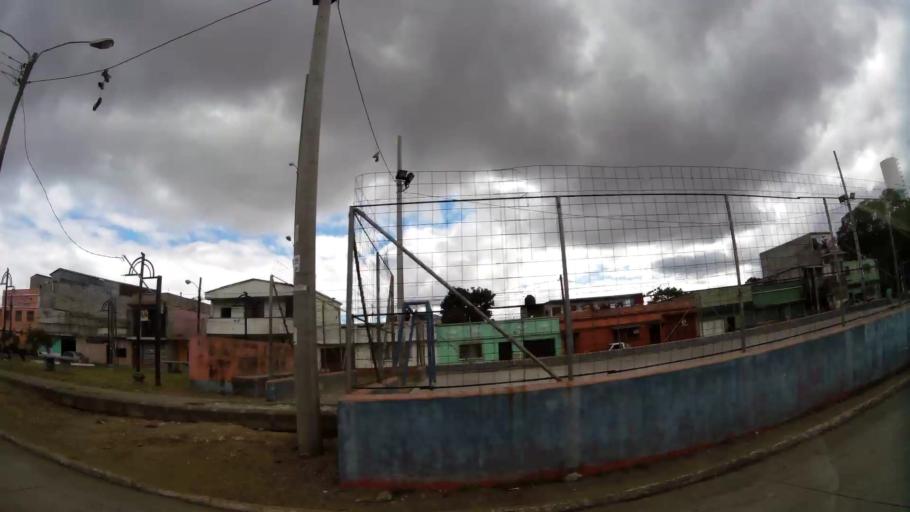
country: GT
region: Guatemala
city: Mixco
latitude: 14.6545
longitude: -90.5731
